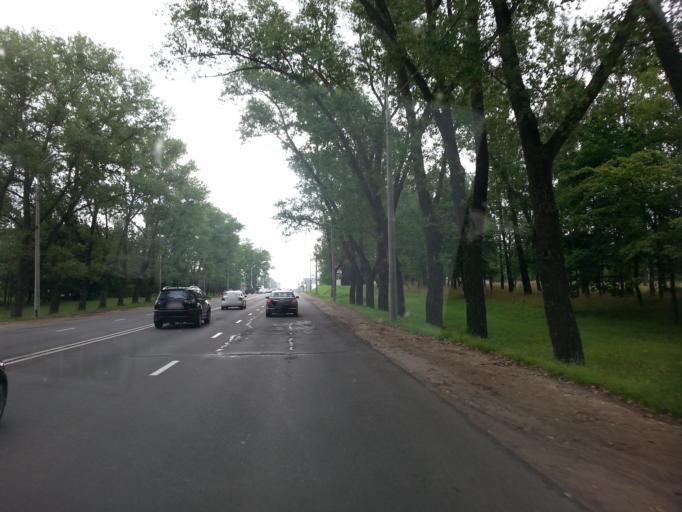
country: BY
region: Minsk
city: Zhdanovichy
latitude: 53.9313
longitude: 27.4694
